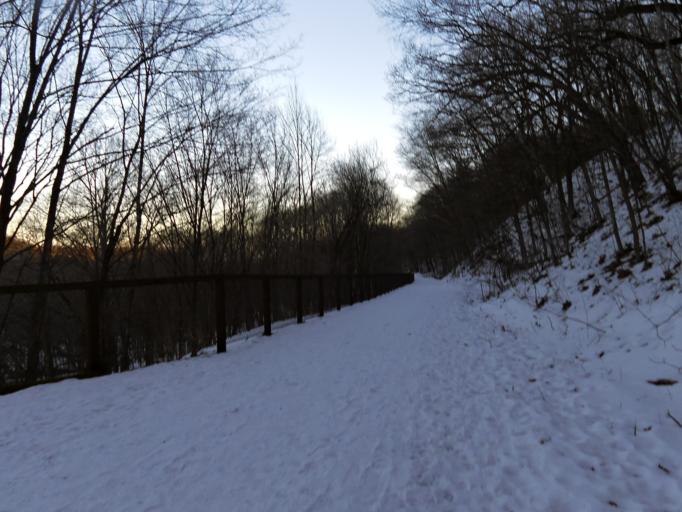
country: US
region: Minnesota
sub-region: Washington County
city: Stillwater
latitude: 45.0755
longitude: -92.8183
